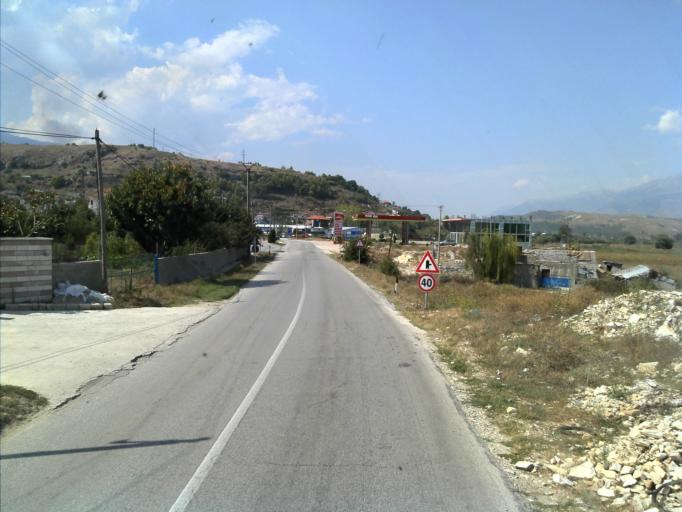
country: AL
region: Gjirokaster
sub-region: Rrethi i Gjirokastres
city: Dervician
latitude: 40.0544
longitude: 20.1764
